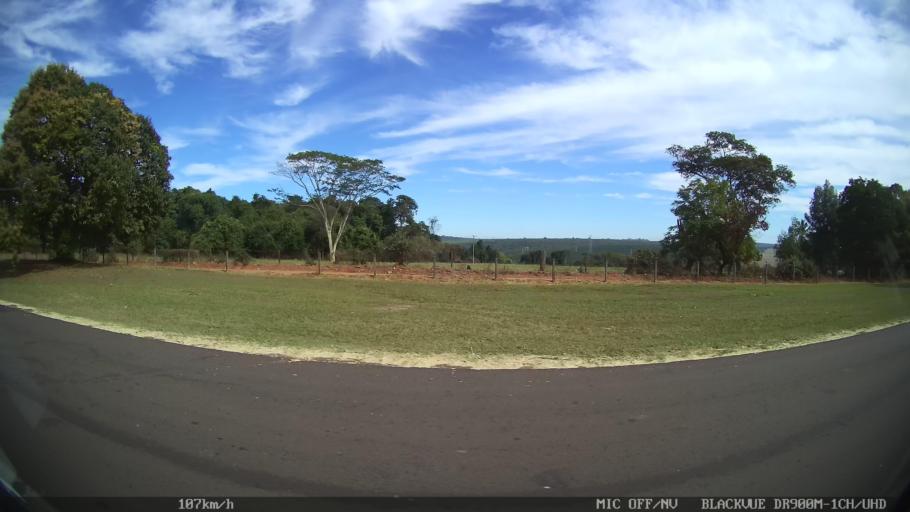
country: BR
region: Sao Paulo
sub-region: Matao
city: Matao
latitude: -21.5976
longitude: -48.4365
